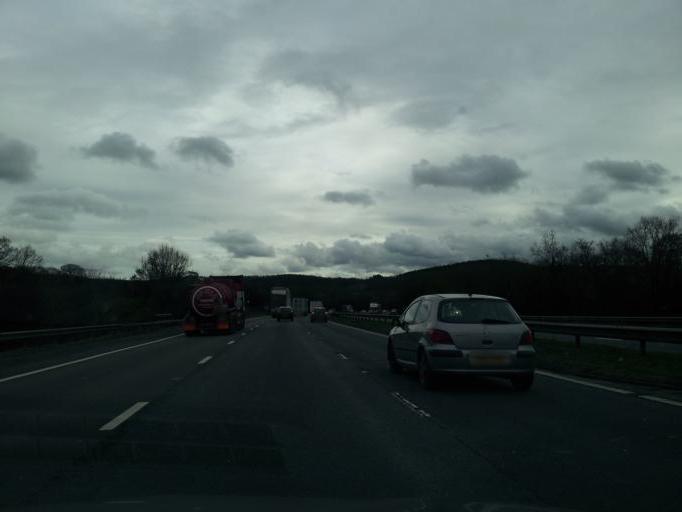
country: GB
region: England
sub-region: Staffordshire
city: Audley
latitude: 53.0275
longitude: -2.3239
